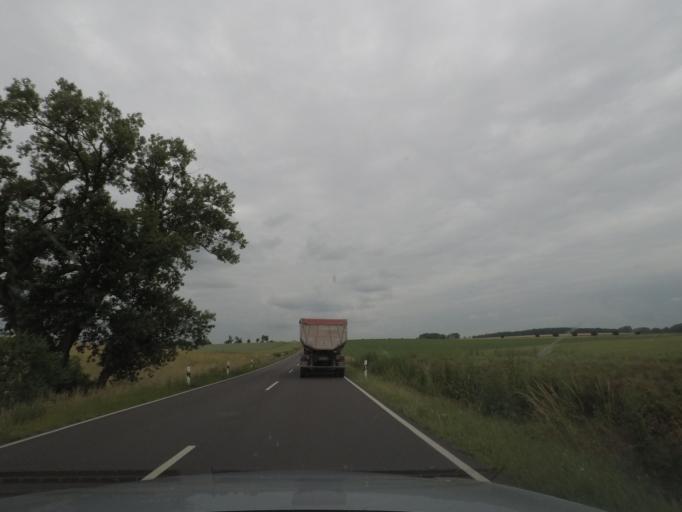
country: DE
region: Saxony-Anhalt
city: Suplingen
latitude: 52.2249
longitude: 11.3085
